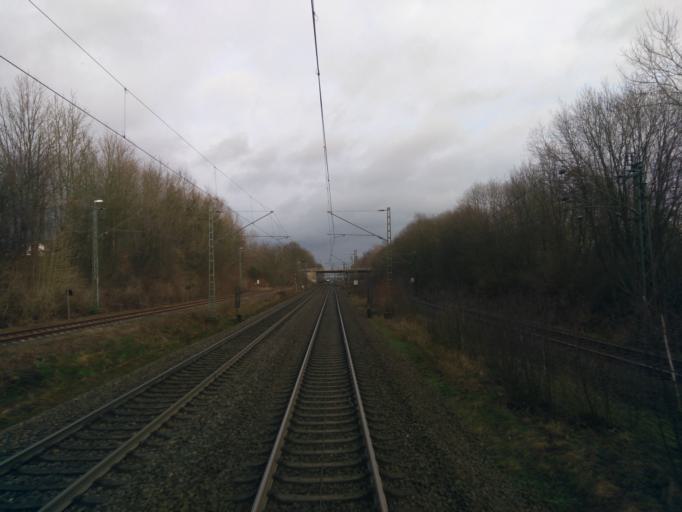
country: DE
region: Lower Saxony
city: Tostedt
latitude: 53.2676
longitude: 9.7224
